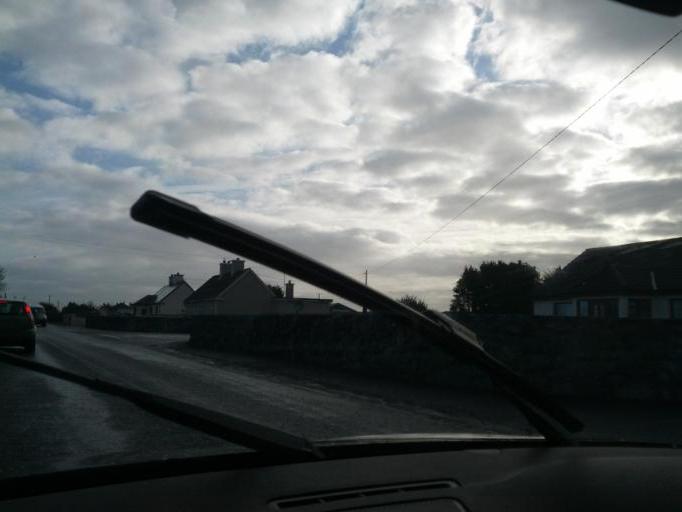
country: IE
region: Connaught
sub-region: County Galway
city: Oranmore
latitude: 53.3187
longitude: -8.8623
